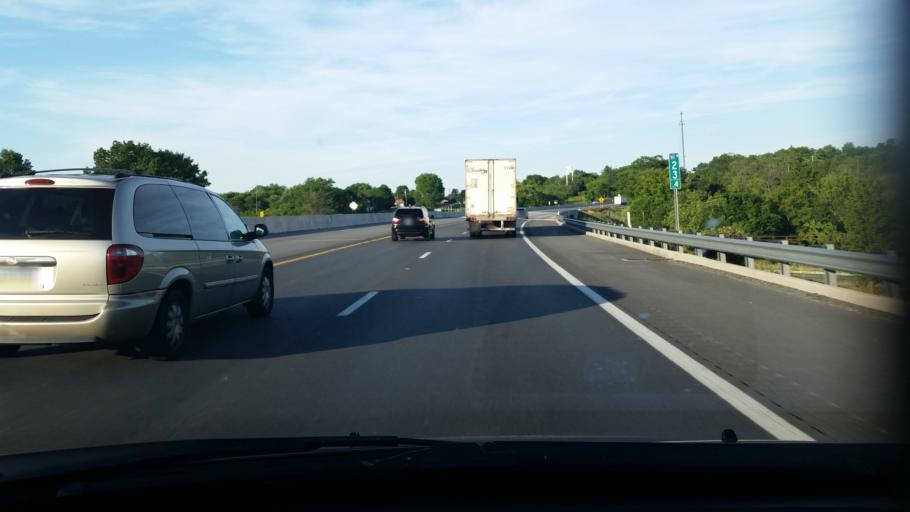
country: US
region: Maryland
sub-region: Washington County
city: Williamsport
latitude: 39.5792
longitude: -77.8783
